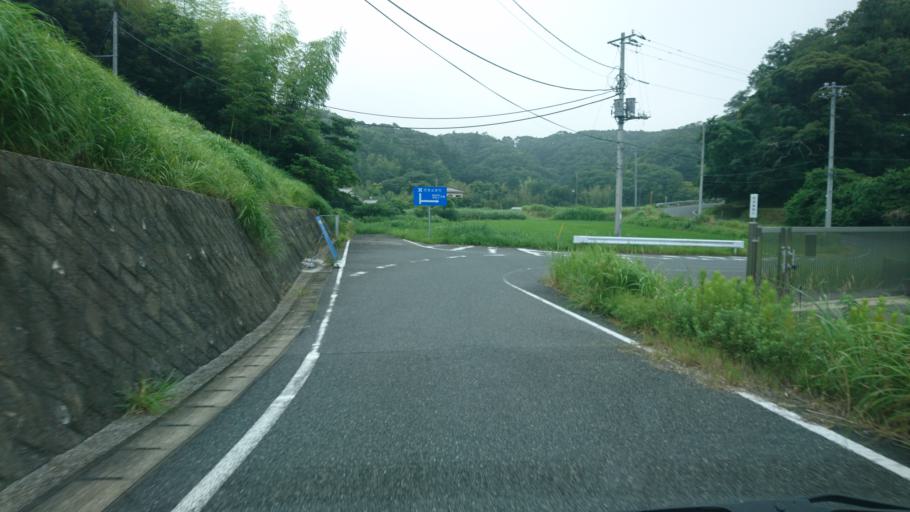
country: JP
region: Chiba
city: Kimitsu
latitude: 35.2828
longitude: 139.9275
